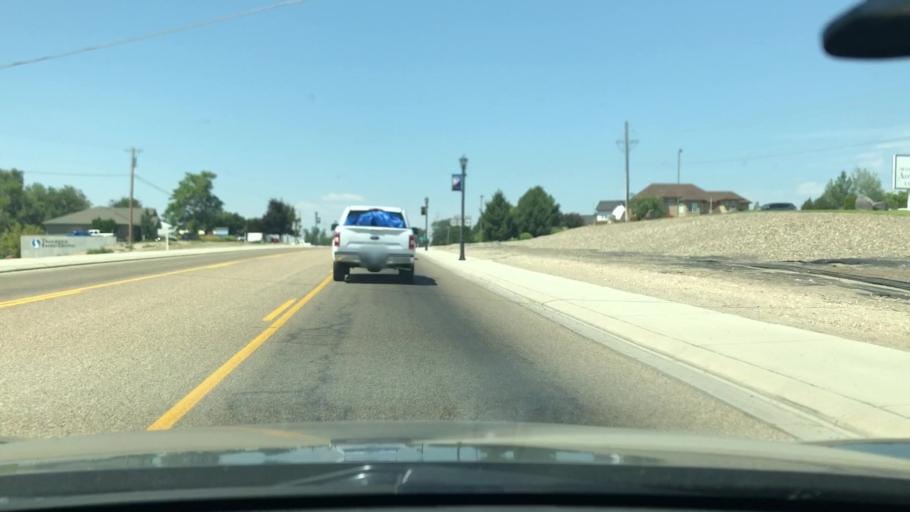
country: US
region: Idaho
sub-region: Canyon County
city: Parma
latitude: 43.7887
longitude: -116.9483
